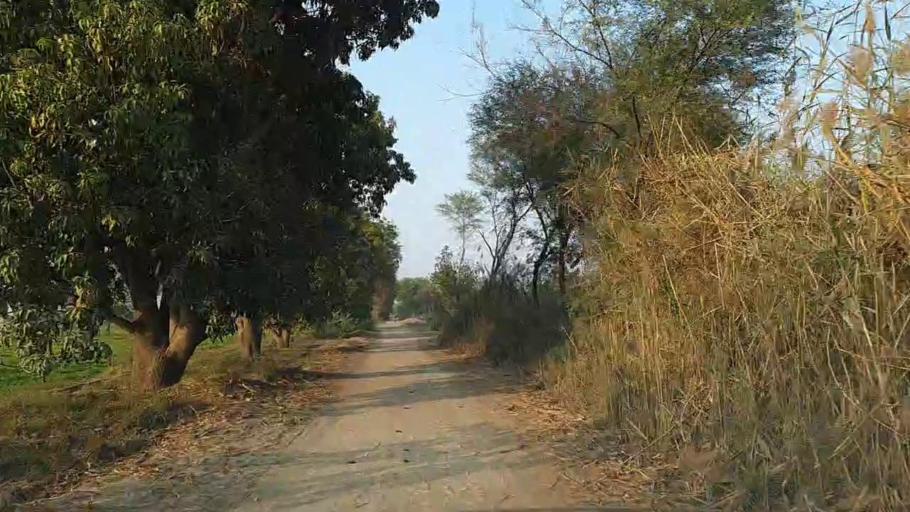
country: PK
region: Sindh
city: Daur
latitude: 26.4350
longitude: 68.3937
